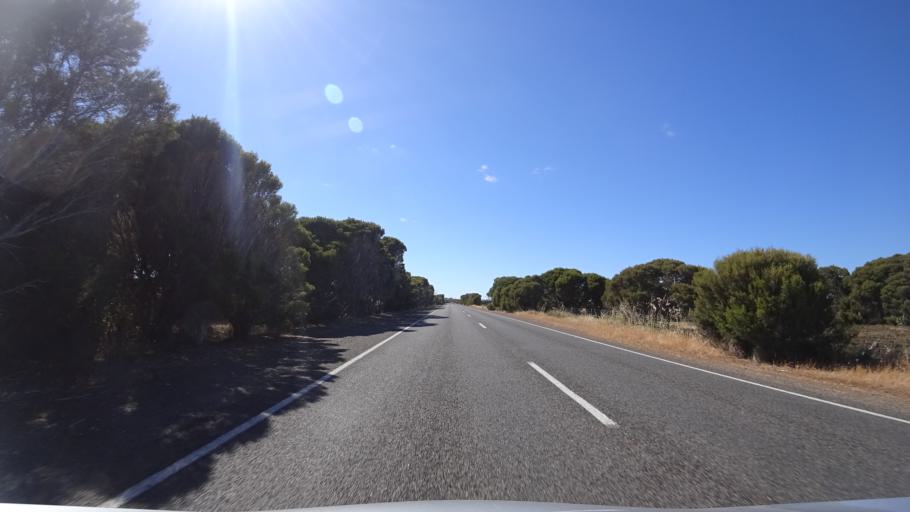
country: AU
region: South Australia
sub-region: Kangaroo Island
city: Kingscote
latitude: -35.7358
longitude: 137.5731
